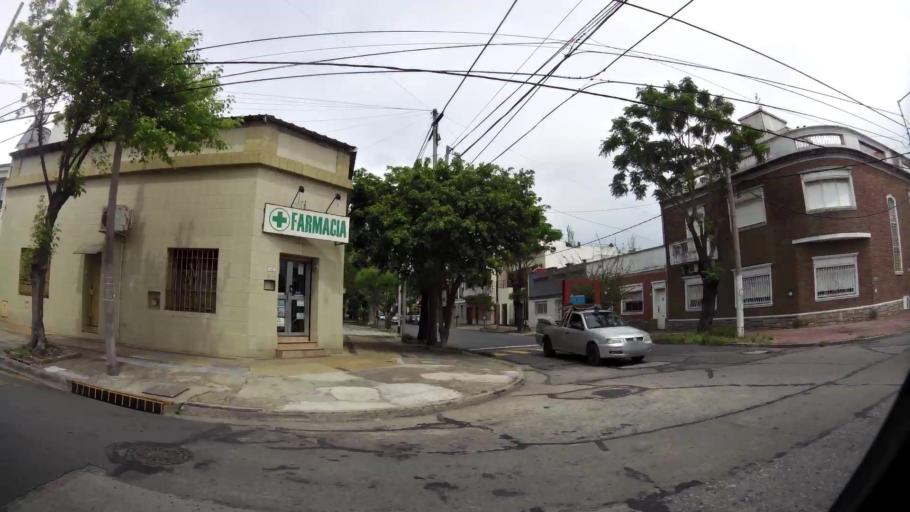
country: AR
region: Buenos Aires
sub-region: Partido de Avellaneda
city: Avellaneda
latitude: -34.6714
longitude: -58.3579
